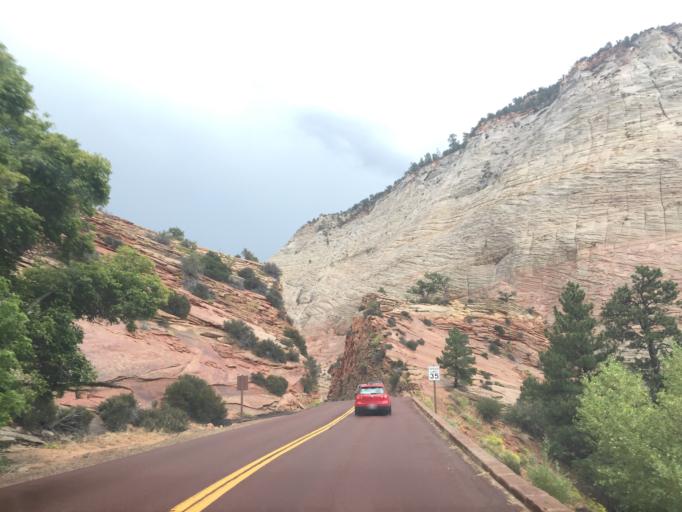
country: US
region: Utah
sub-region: Washington County
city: Hildale
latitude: 37.2250
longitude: -112.8954
